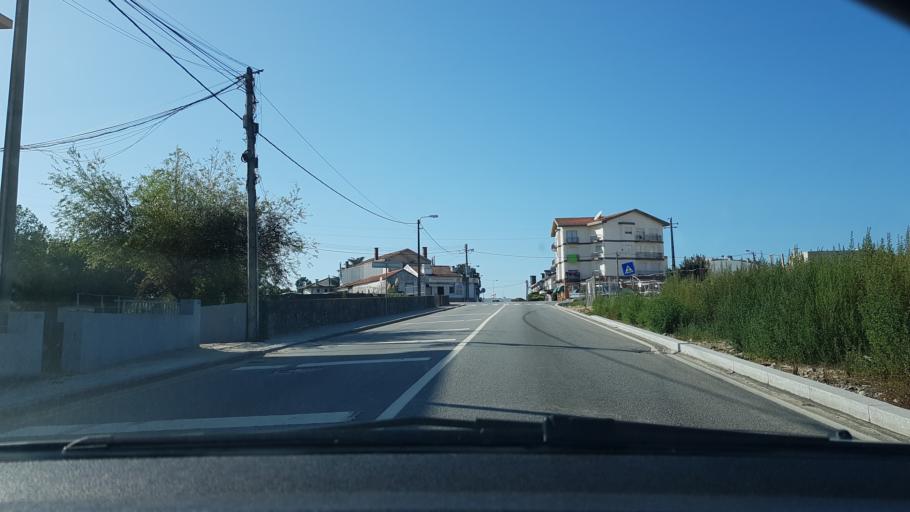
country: PT
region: Porto
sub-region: Gondomar
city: Baguim do Monte
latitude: 41.1836
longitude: -8.5383
